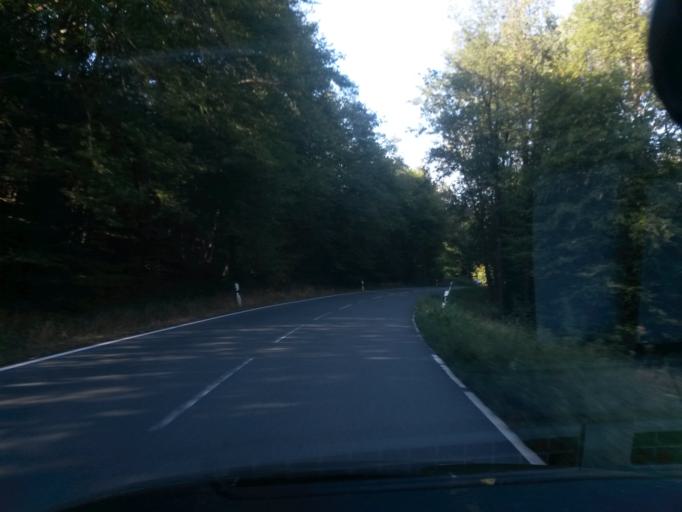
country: DE
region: North Rhine-Westphalia
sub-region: Regierungsbezirk Koln
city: Numbrecht
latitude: 50.9056
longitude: 7.5239
